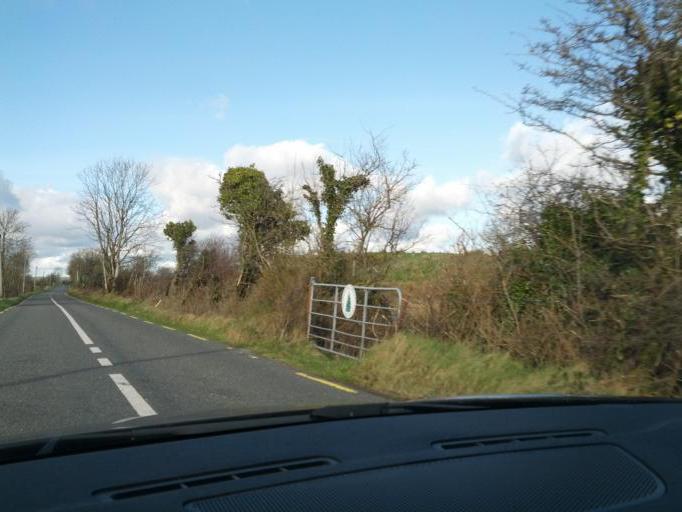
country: IE
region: Connaught
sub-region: Roscommon
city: Castlerea
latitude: 53.5064
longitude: -8.5713
